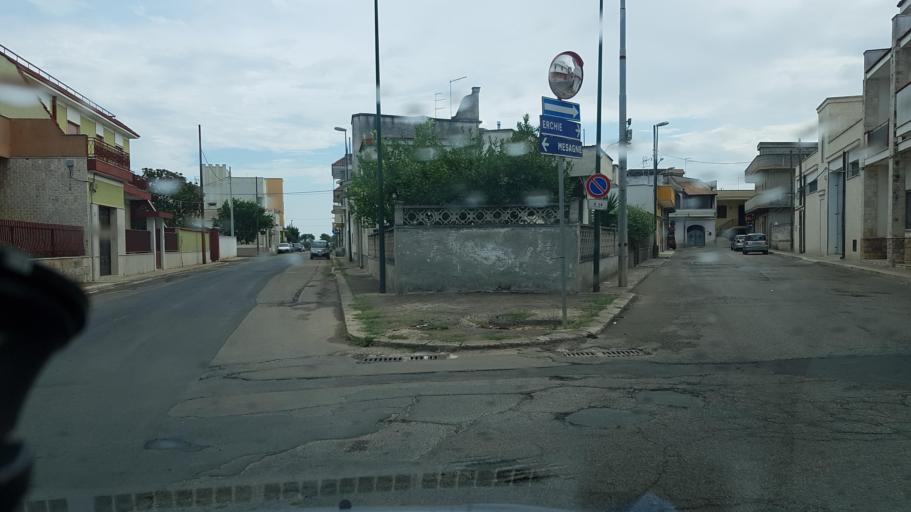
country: IT
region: Apulia
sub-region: Provincia di Brindisi
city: Torre Santa Susanna
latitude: 40.4617
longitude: 17.7437
